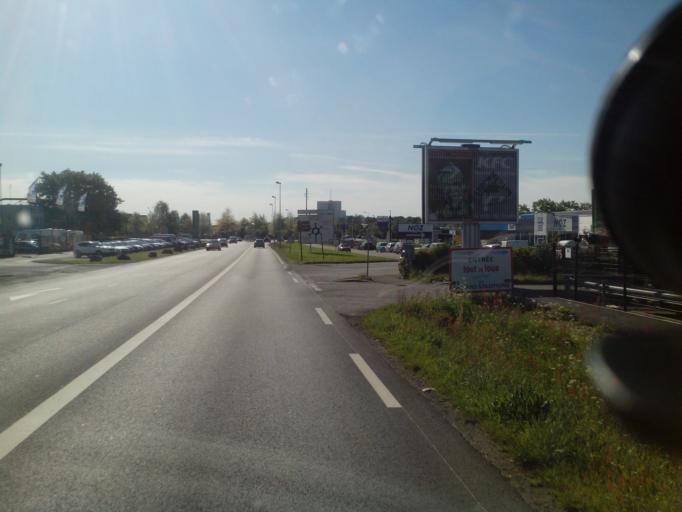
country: FR
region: Pays de la Loire
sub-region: Departement de la Loire-Atlantique
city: Orvault
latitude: 47.2526
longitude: -1.6241
